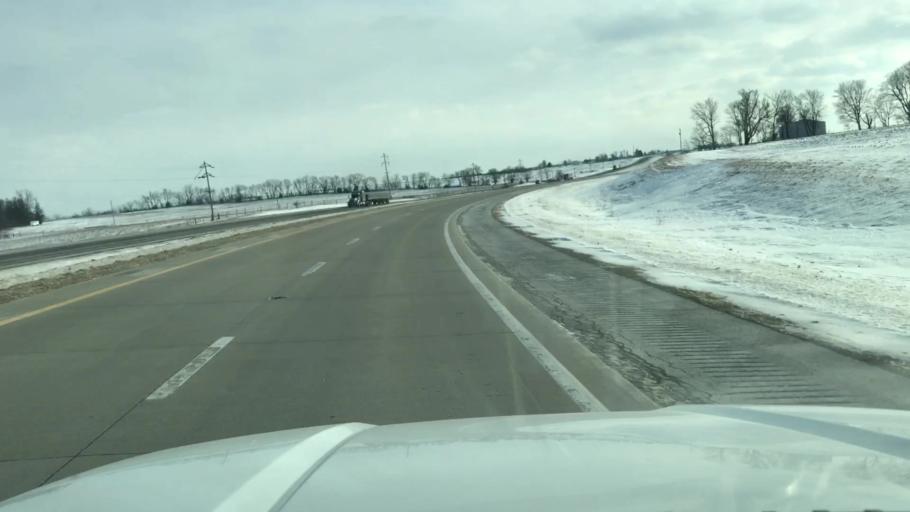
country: US
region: Missouri
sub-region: Nodaway County
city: Maryville
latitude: 40.2716
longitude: -94.8672
